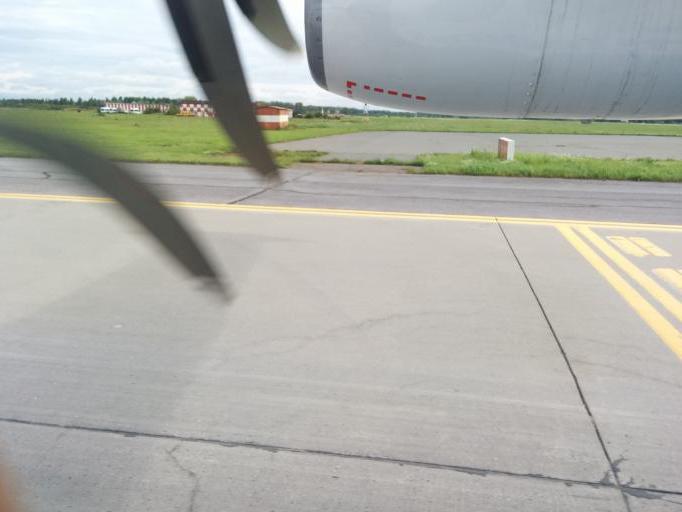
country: RU
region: Perm
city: Kultayevo
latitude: 57.9173
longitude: 56.0239
